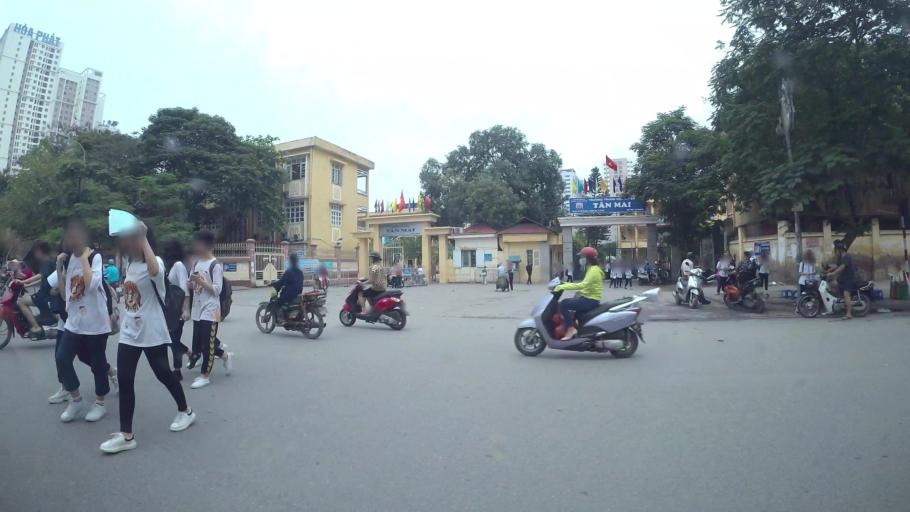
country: VN
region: Ha Noi
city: Hai BaTrung
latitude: 20.9837
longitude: 105.8500
